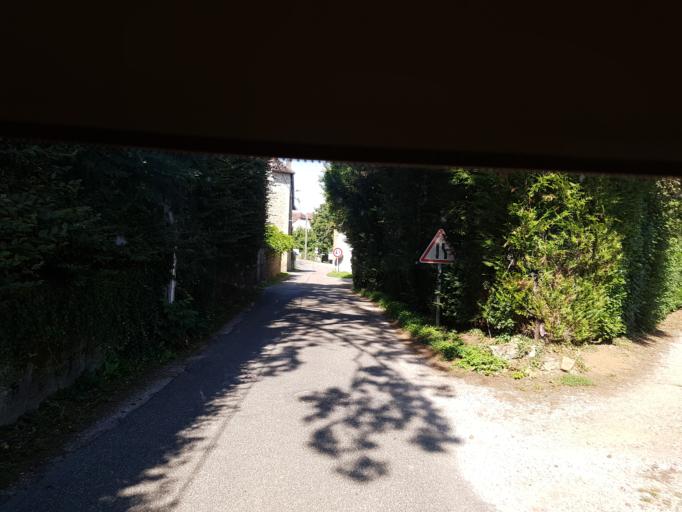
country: FR
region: Franche-Comte
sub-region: Departement du Jura
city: Perrigny
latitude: 46.7289
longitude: 5.5849
